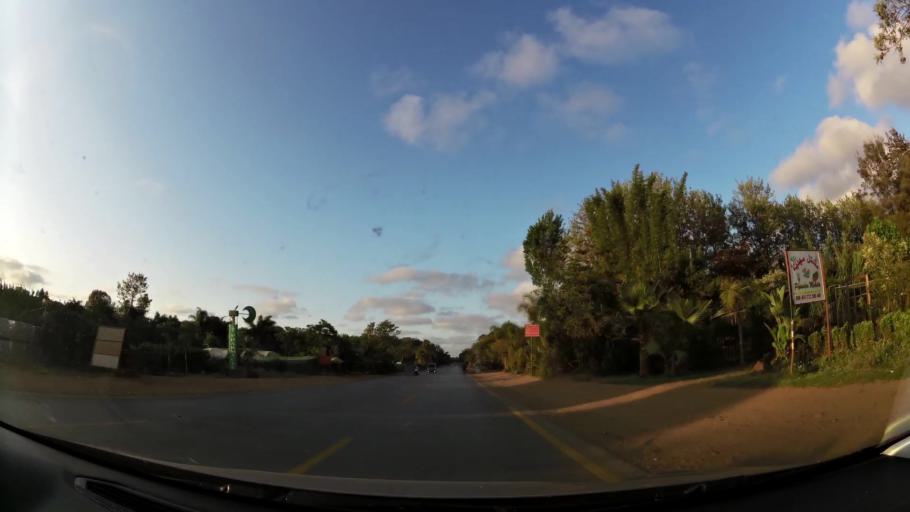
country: MA
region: Gharb-Chrarda-Beni Hssen
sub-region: Kenitra Province
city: Kenitra
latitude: 34.2115
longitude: -6.6701
